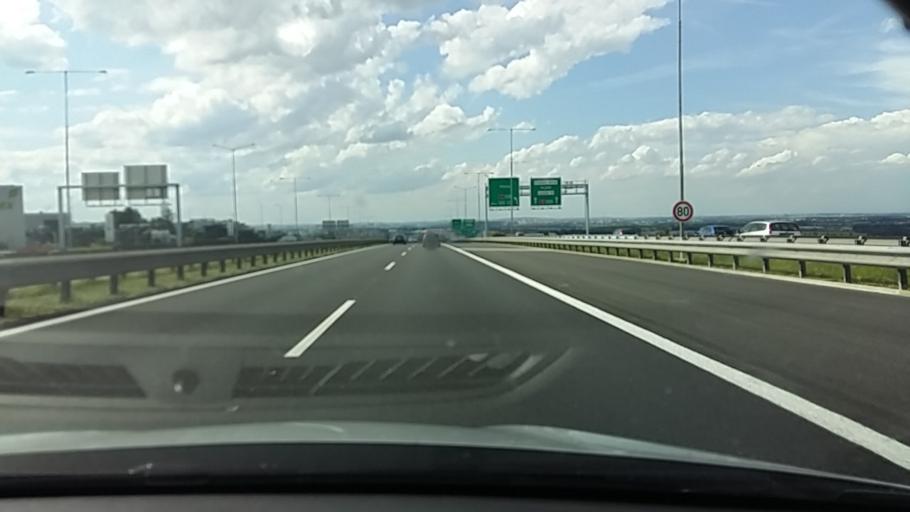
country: CZ
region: Central Bohemia
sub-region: Okres Praha-Vychod
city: Ricany
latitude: 49.9752
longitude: 14.6132
